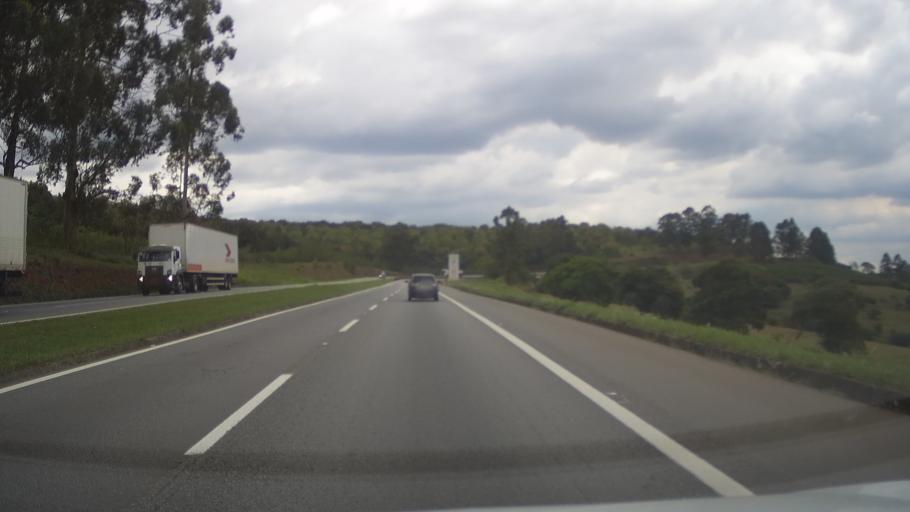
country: BR
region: Minas Gerais
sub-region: Tres Coracoes
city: Tres Coracoes
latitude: -21.5048
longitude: -45.2151
